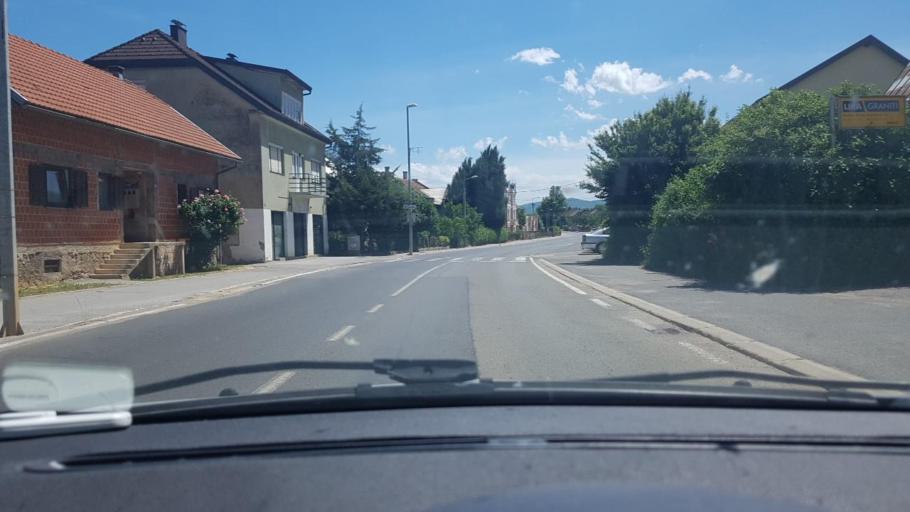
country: HR
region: Licko-Senjska
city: Otocac
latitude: 44.8693
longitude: 15.2431
